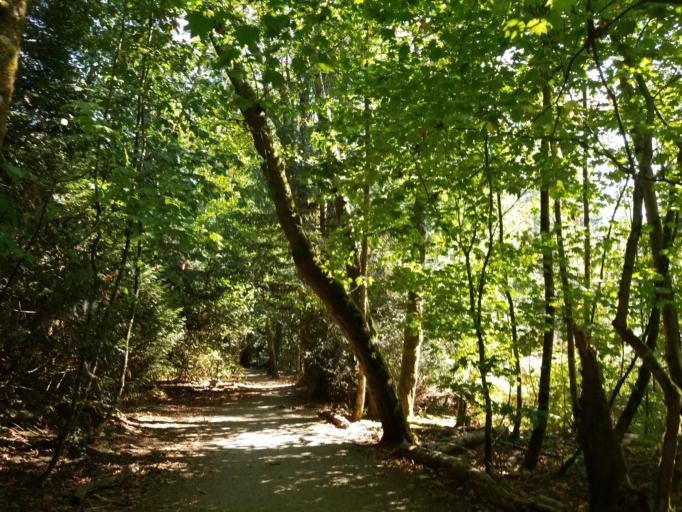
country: CA
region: British Columbia
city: West End
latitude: 49.2506
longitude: -123.2089
